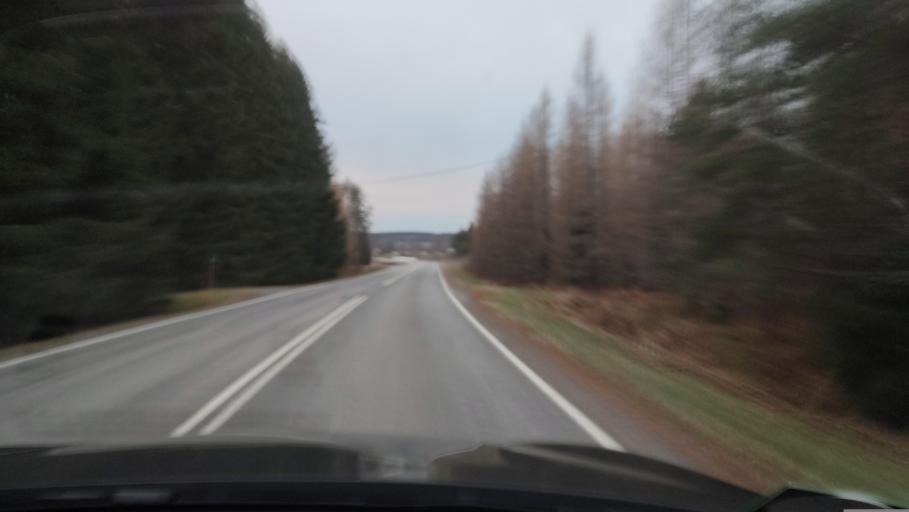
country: FI
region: Southern Ostrobothnia
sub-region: Suupohja
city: Karijoki
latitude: 62.3233
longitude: 21.7550
